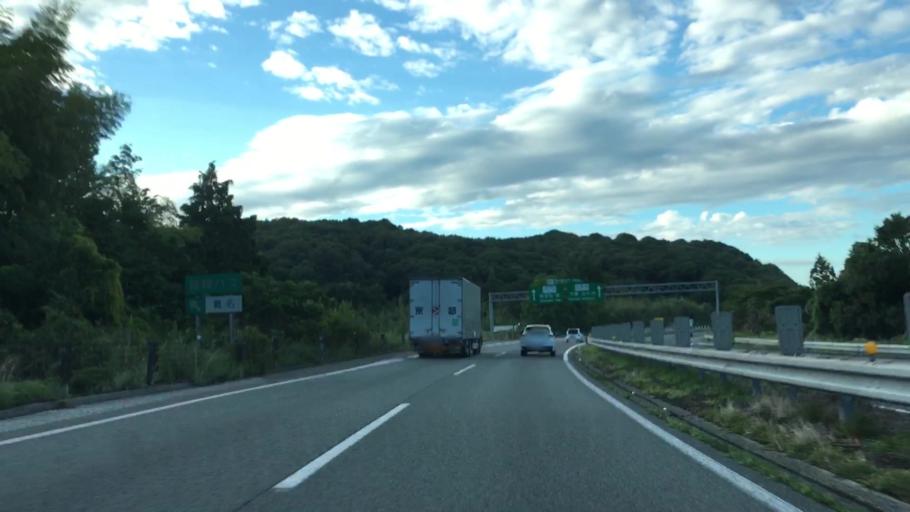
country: JP
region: Yamaguchi
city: Ogori-shimogo
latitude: 34.1637
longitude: 131.3265
